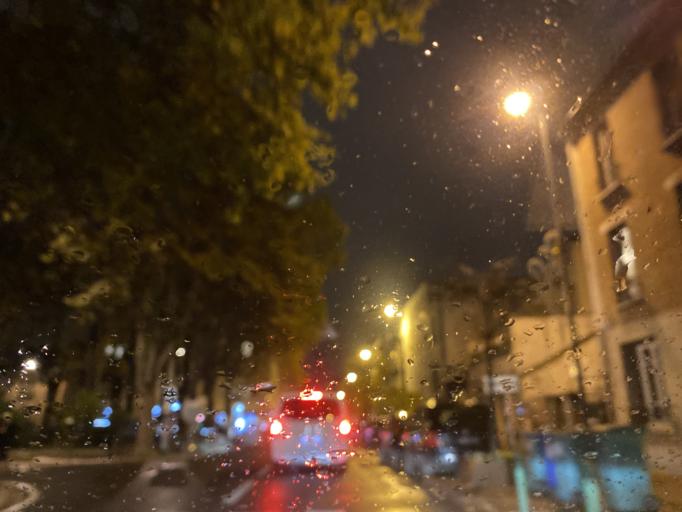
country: FR
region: Ile-de-France
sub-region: Departement des Hauts-de-Seine
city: Malakoff
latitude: 48.8192
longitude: 2.3008
